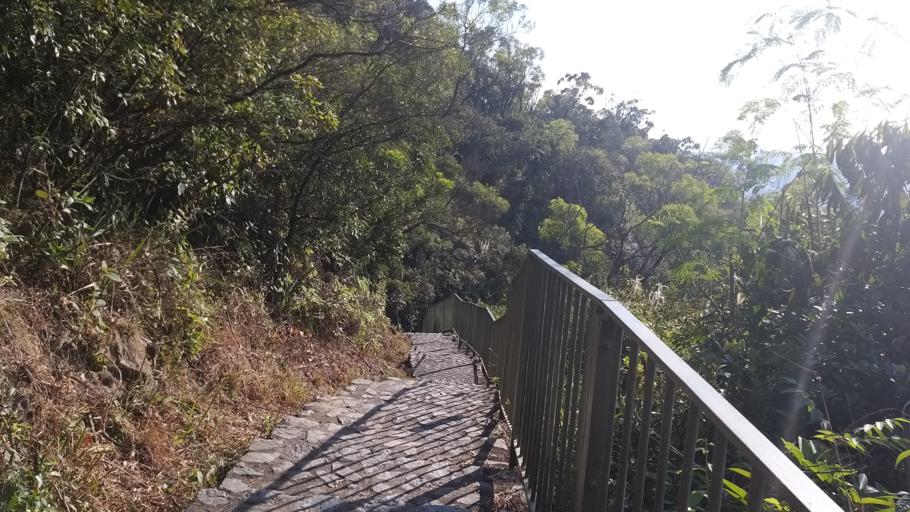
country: HK
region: Tuen Mun
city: Tuen Mun
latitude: 22.3971
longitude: 113.9836
